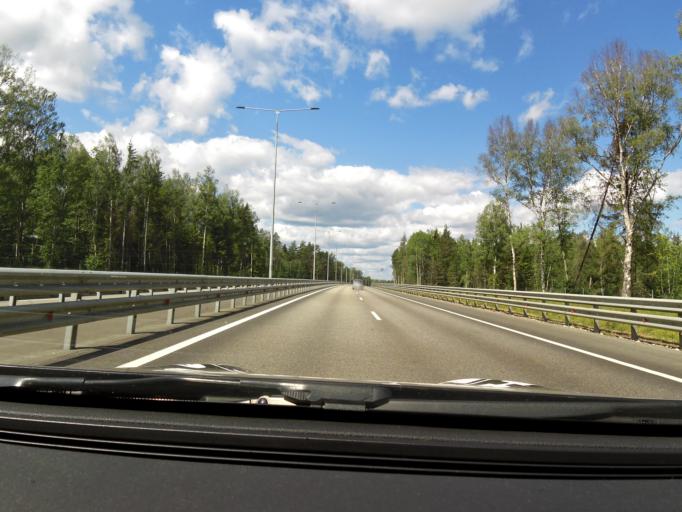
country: RU
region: Tverskaya
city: Vyshniy Volochek
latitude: 57.3768
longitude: 34.5839
